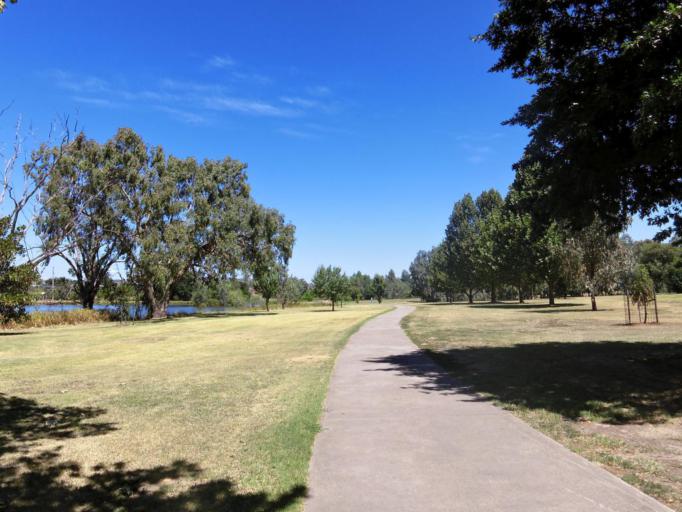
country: AU
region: Victoria
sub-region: Wodonga
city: Wodonga
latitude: -36.1124
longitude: 146.8889
